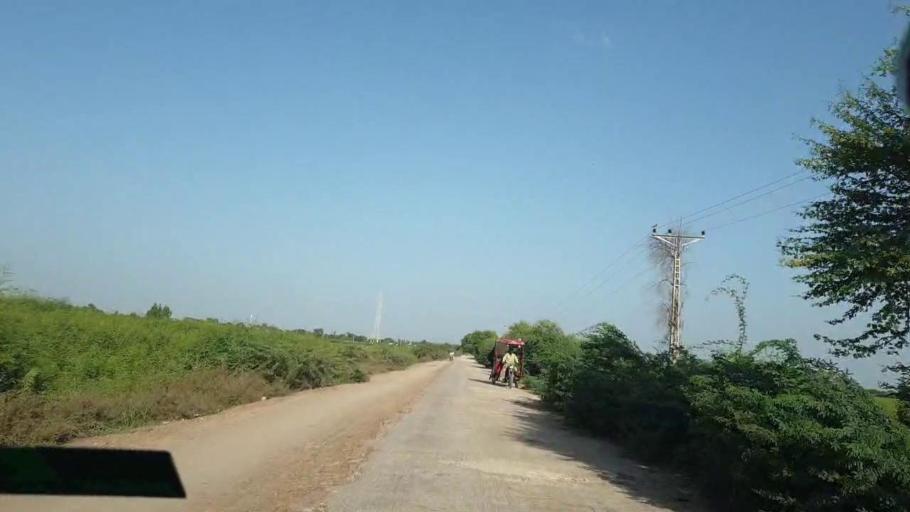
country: PK
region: Sindh
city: Naukot
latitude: 24.7378
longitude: 69.2163
